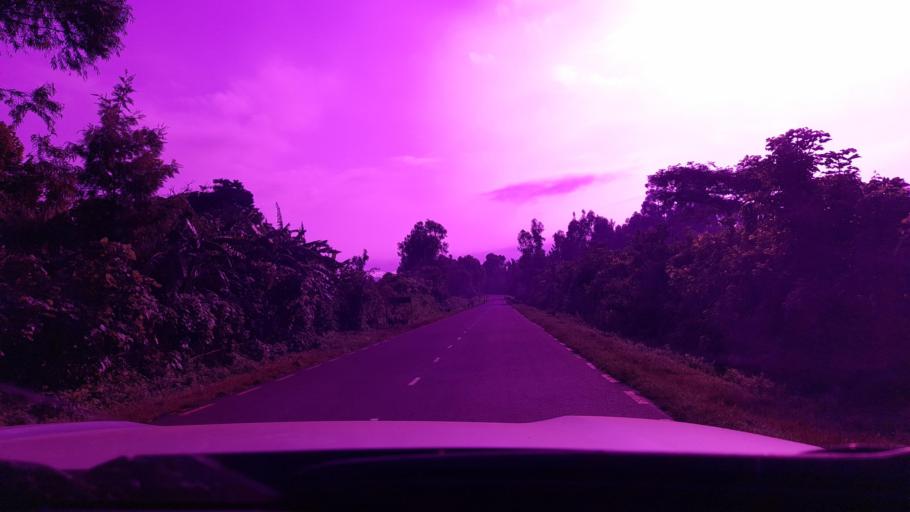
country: ET
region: Oromiya
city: Bedele
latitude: 8.1544
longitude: 36.4712
